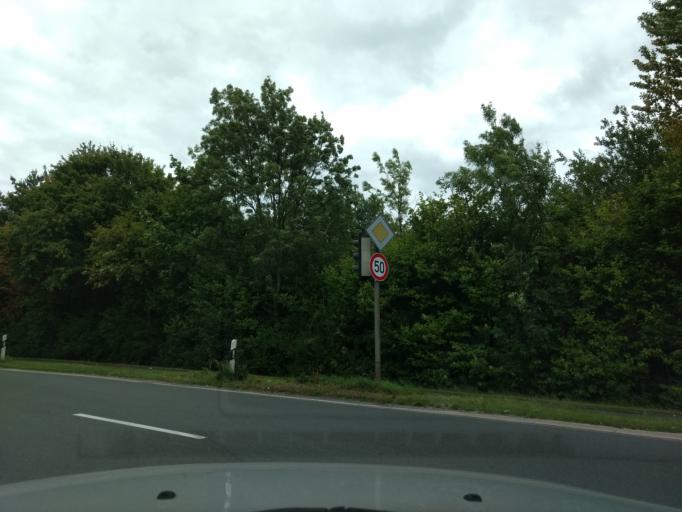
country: DE
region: North Rhine-Westphalia
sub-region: Regierungsbezirk Dusseldorf
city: Ratingen
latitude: 51.2977
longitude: 6.8087
